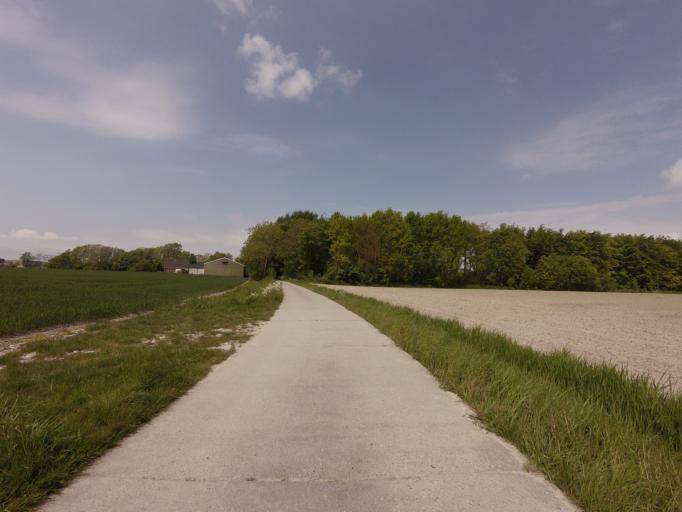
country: NL
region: Friesland
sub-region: Sudwest Fryslan
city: Bolsward
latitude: 53.1089
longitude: 5.4814
